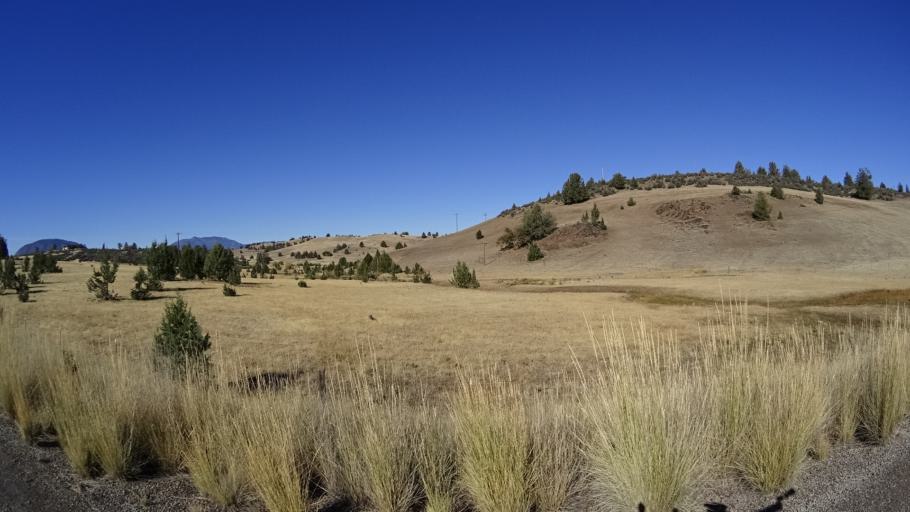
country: US
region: California
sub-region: Siskiyou County
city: Montague
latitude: 41.9050
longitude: -122.3807
